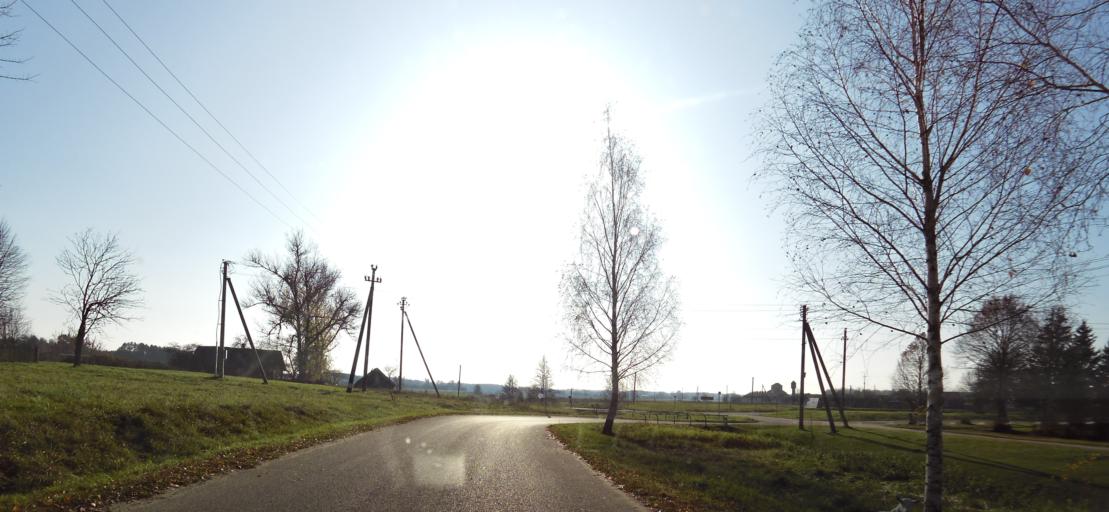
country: LT
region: Vilnius County
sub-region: Trakai
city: Rudiskes
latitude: 54.4948
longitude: 24.6781
